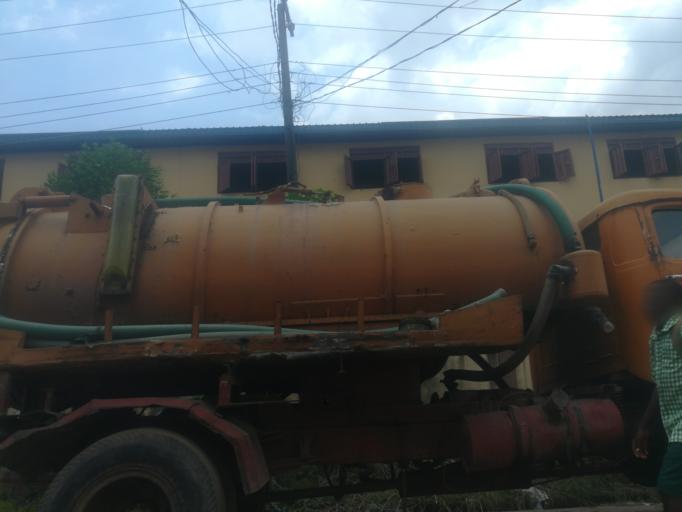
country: NG
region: Lagos
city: Ojota
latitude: 6.5617
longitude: 3.3919
